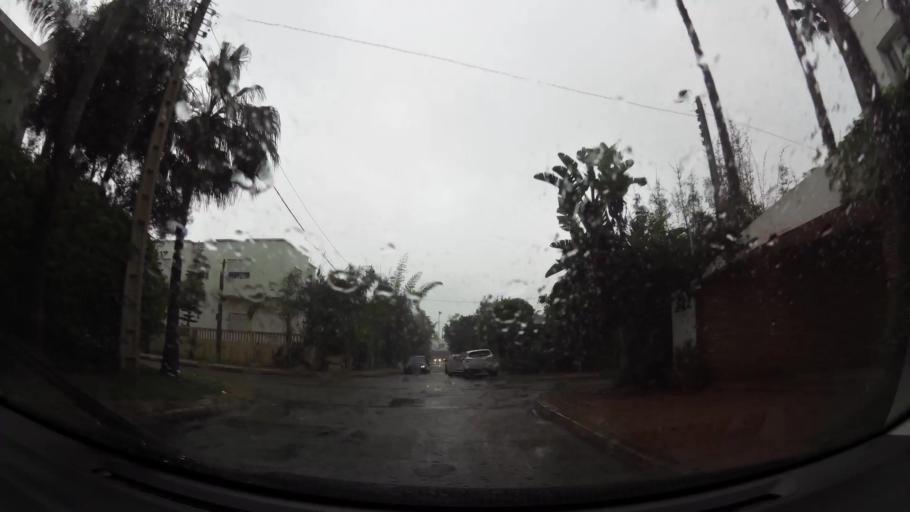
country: MA
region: Grand Casablanca
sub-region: Casablanca
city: Casablanca
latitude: 33.5875
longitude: -7.6777
